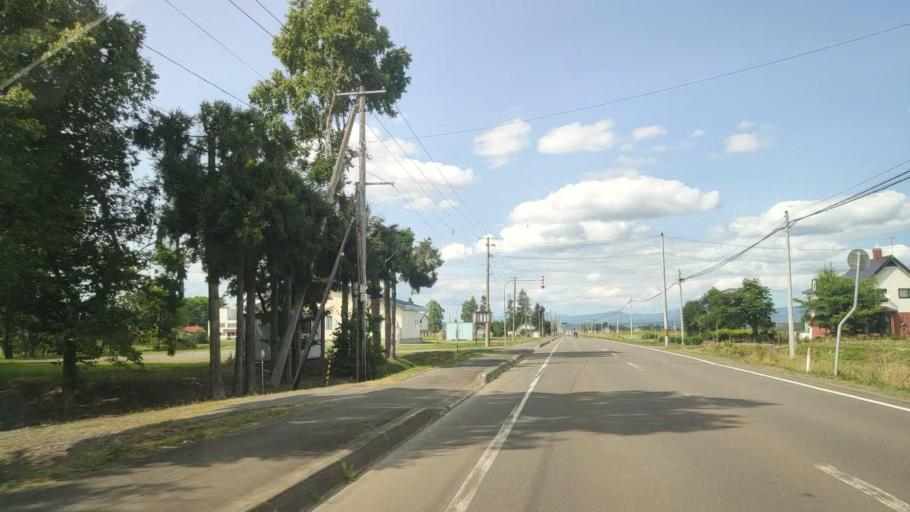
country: JP
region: Hokkaido
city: Nayoro
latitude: 44.2887
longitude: 142.4294
